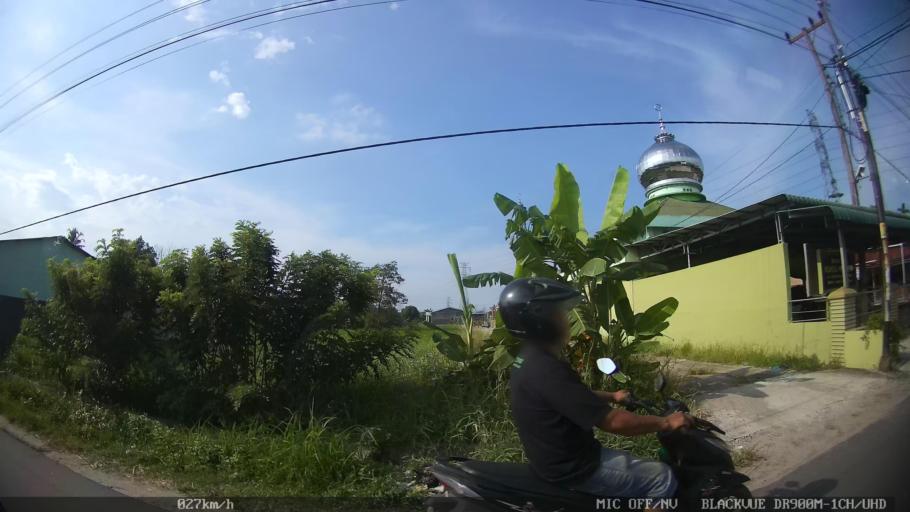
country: ID
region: North Sumatra
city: Percut
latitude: 3.5940
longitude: 98.7878
